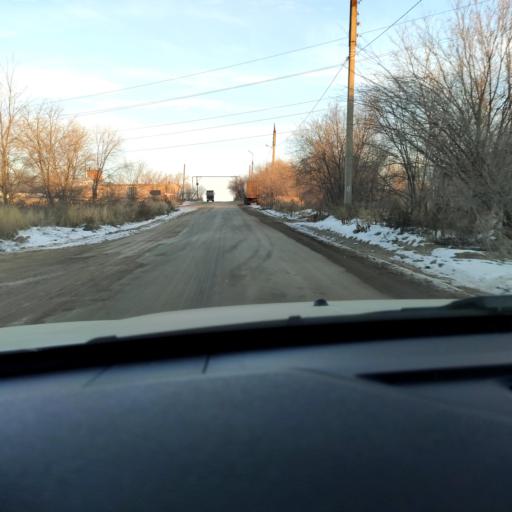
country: RU
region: Samara
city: Smyshlyayevka
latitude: 53.2386
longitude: 50.4806
